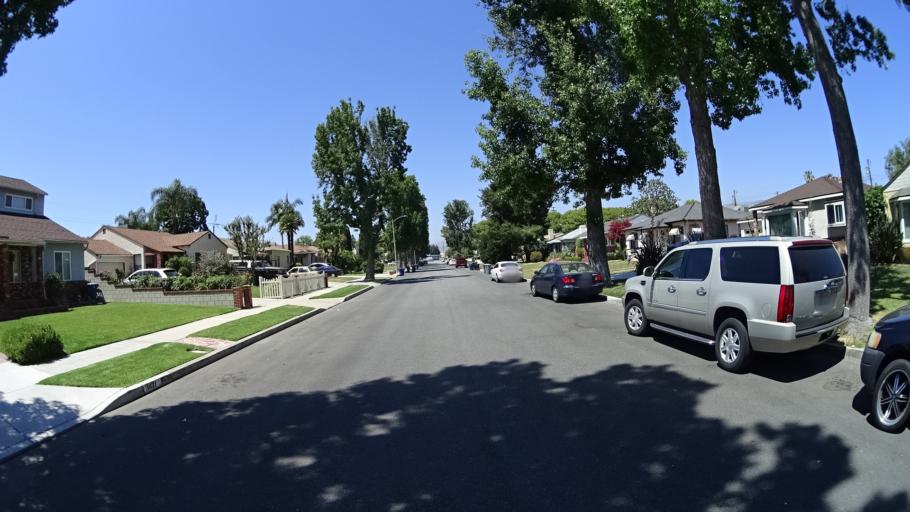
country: US
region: California
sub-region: Los Angeles County
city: North Hollywood
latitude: 34.1748
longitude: -118.3526
